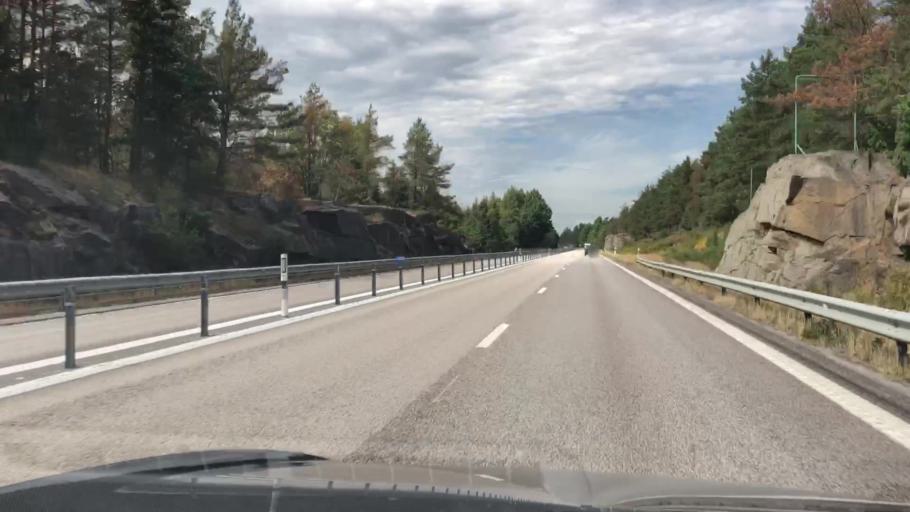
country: SE
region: Blekinge
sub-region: Ronneby Kommun
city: Brakne-Hoby
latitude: 56.2195
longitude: 15.1618
